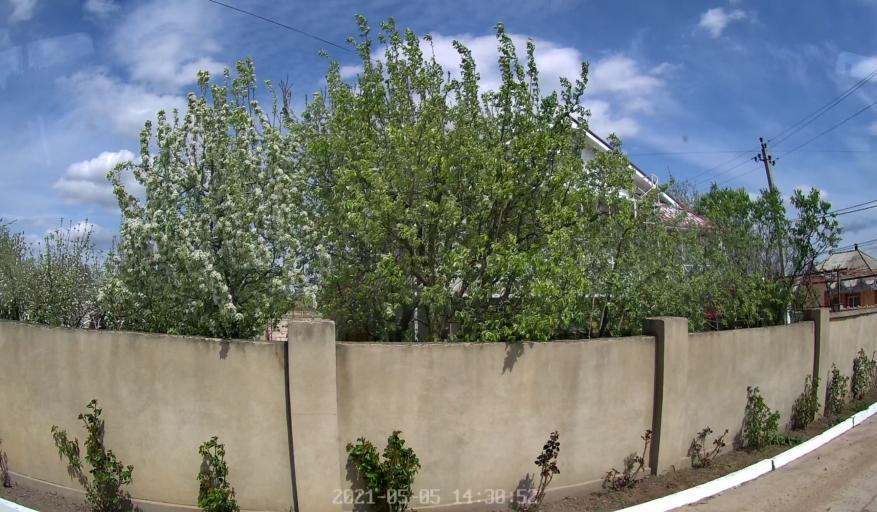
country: MD
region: Chisinau
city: Vadul lui Voda
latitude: 47.0775
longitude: 29.1409
